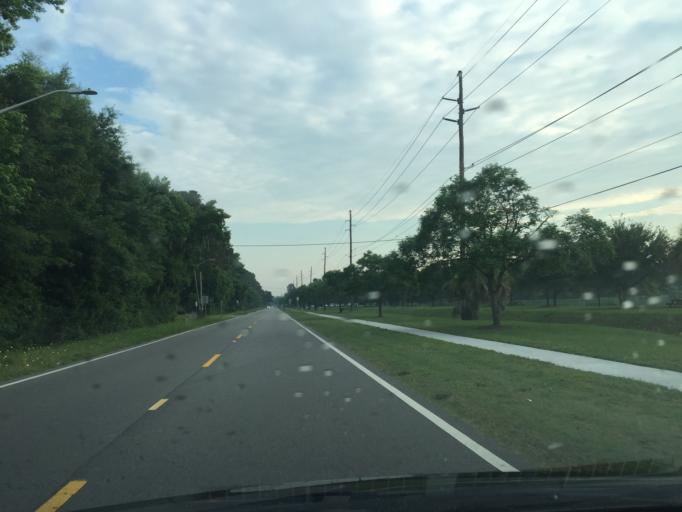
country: US
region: Georgia
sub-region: Chatham County
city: Isle of Hope
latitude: 31.9927
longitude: -81.0905
